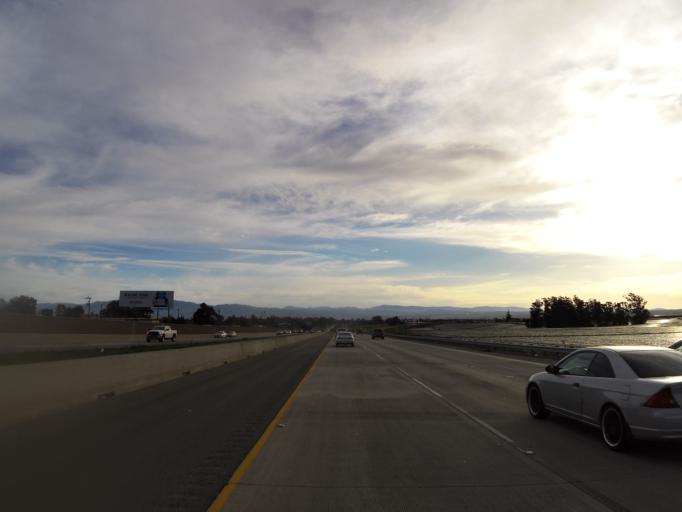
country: US
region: California
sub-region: Monterey County
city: Boronda
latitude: 36.7312
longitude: -121.6575
